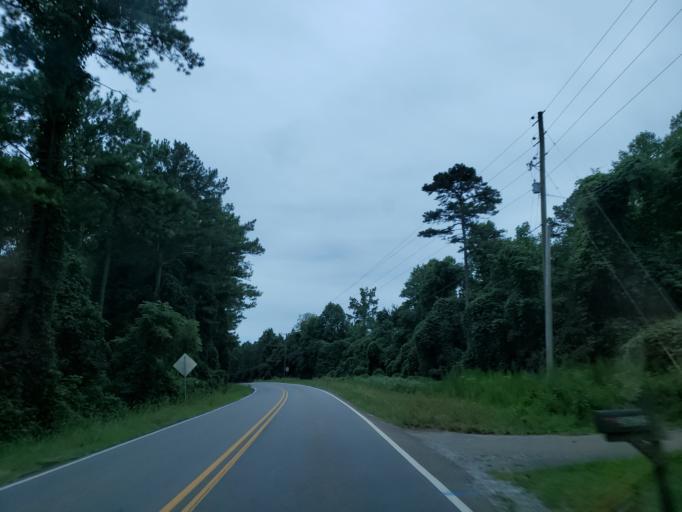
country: US
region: Georgia
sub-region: Cherokee County
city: Canton
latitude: 34.2880
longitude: -84.4541
